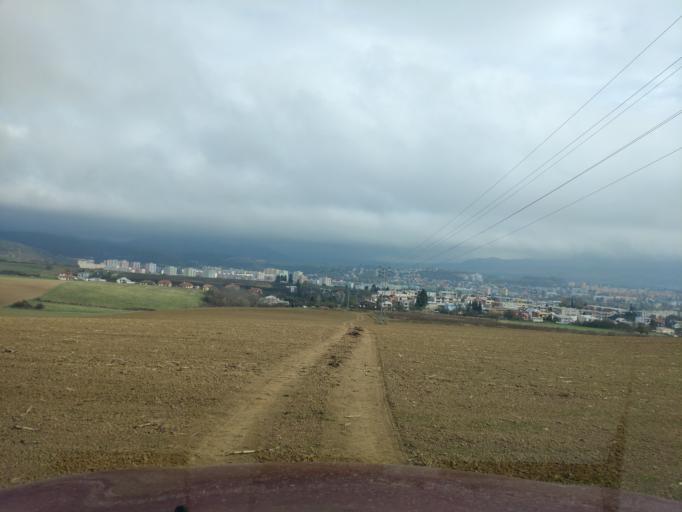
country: SK
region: Presovsky
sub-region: Okres Presov
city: Presov
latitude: 49.0065
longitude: 21.2060
